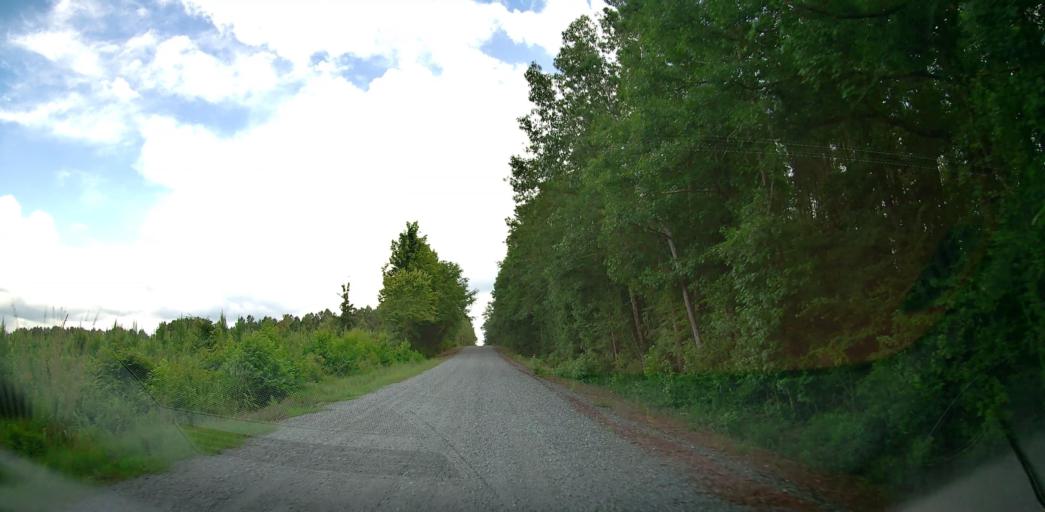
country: US
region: Georgia
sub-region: Bleckley County
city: Cochran
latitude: 32.4246
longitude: -83.4540
